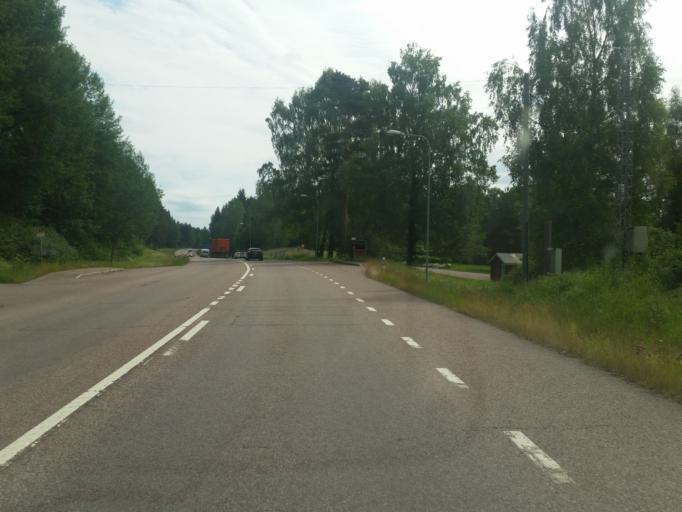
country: SE
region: Dalarna
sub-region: Borlange Kommun
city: Borlaenge
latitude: 60.5304
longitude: 15.3145
